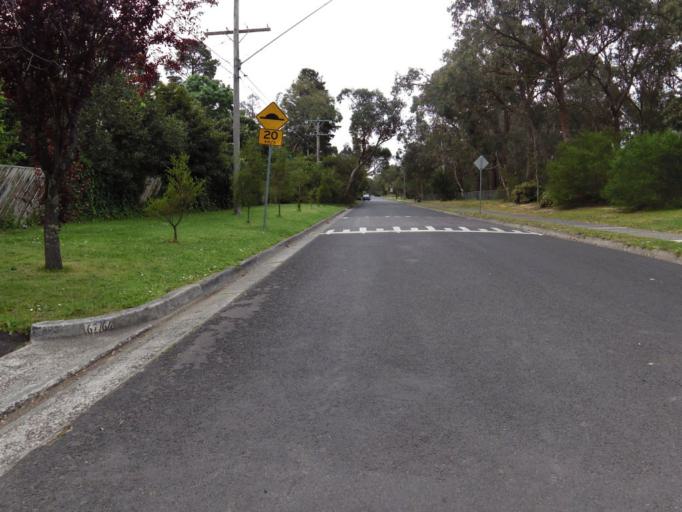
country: AU
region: Victoria
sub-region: Knox
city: Wantirna
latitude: -37.8380
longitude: 145.2303
